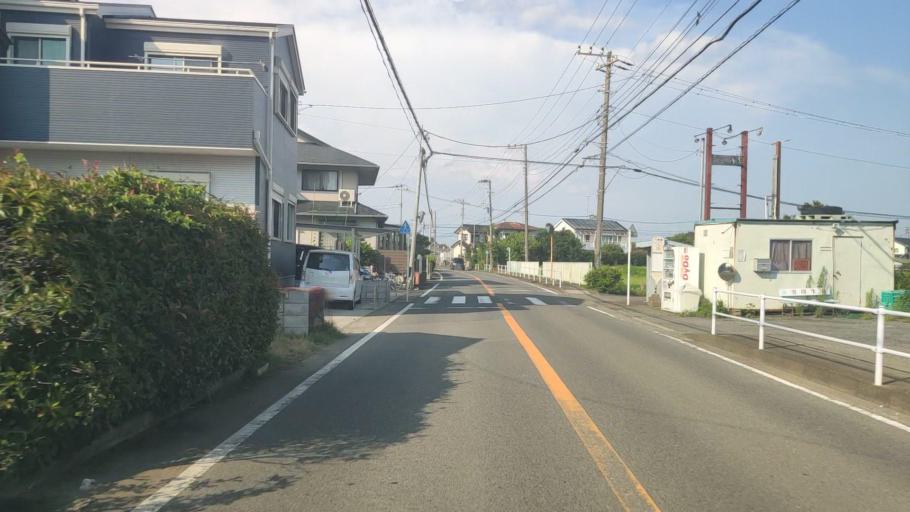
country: JP
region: Kanagawa
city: Isehara
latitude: 35.3763
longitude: 139.3339
